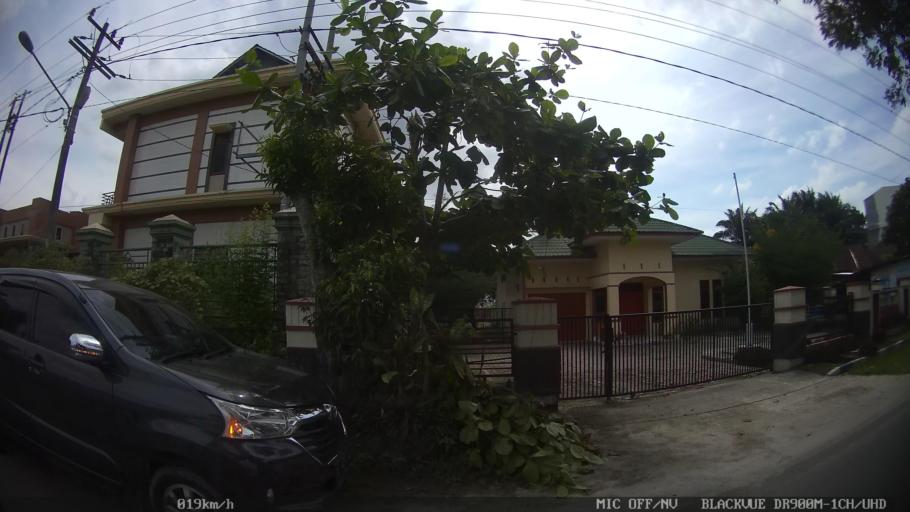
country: ID
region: North Sumatra
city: Percut
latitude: 3.5604
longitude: 98.8668
